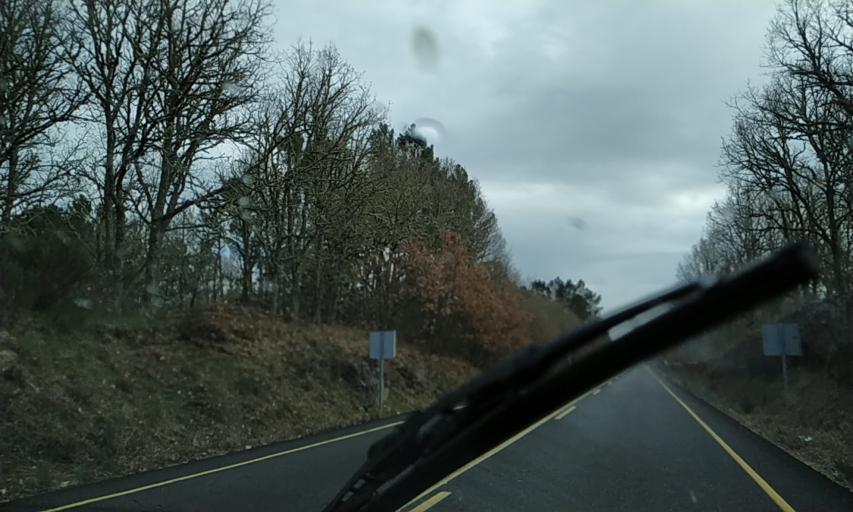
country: ES
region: Castille and Leon
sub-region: Provincia de Salamanca
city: Villasrubias
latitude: 40.3219
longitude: -6.6477
